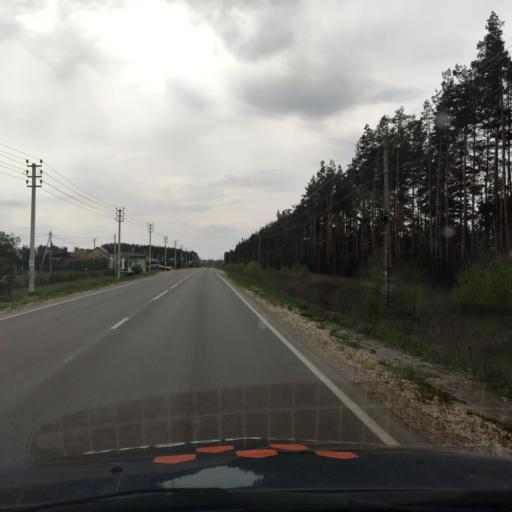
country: RU
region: Voronezj
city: Podgornoye
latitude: 51.8566
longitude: 39.1611
